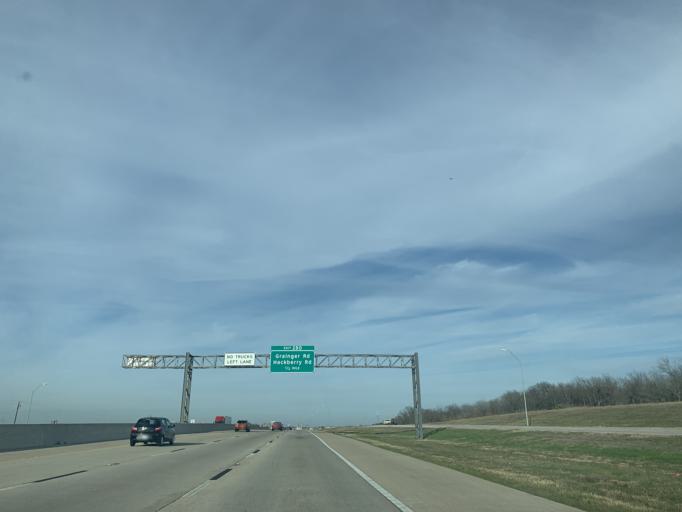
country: US
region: Texas
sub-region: Bell County
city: Salado
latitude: 30.8682
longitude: -97.5839
